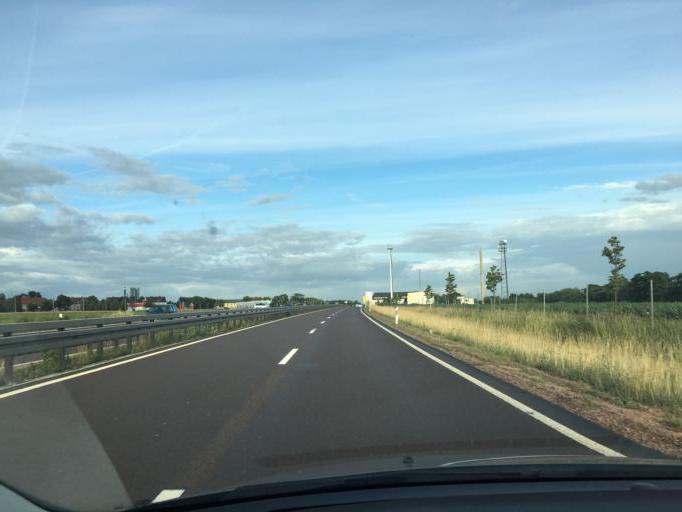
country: DE
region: Saxony-Anhalt
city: Bernburg
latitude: 51.8097
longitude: 11.7171
